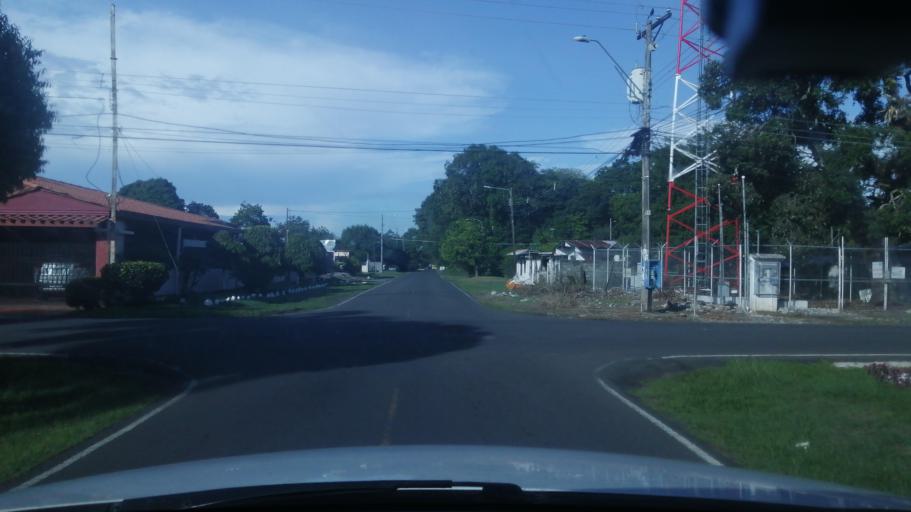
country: PA
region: Chiriqui
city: David
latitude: 8.4375
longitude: -82.4320
